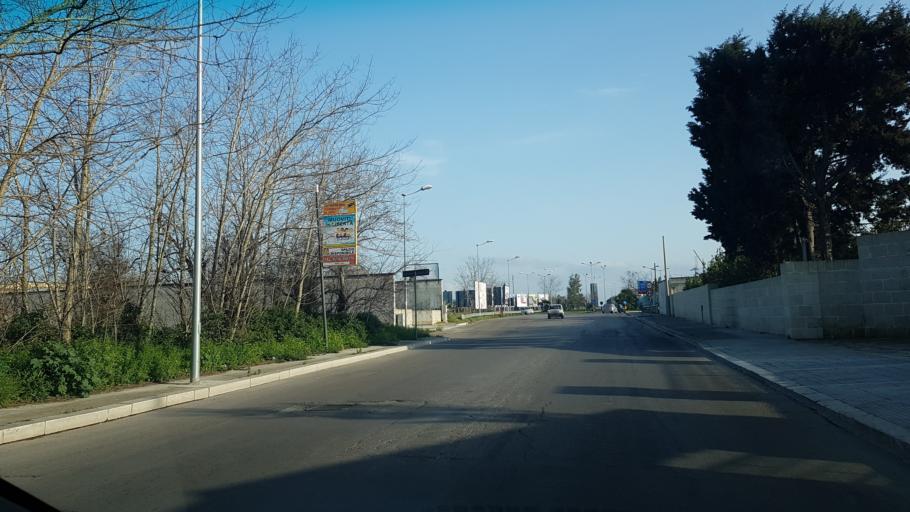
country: IT
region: Apulia
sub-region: Provincia di Lecce
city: Squinzano
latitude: 40.4288
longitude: 18.0521
